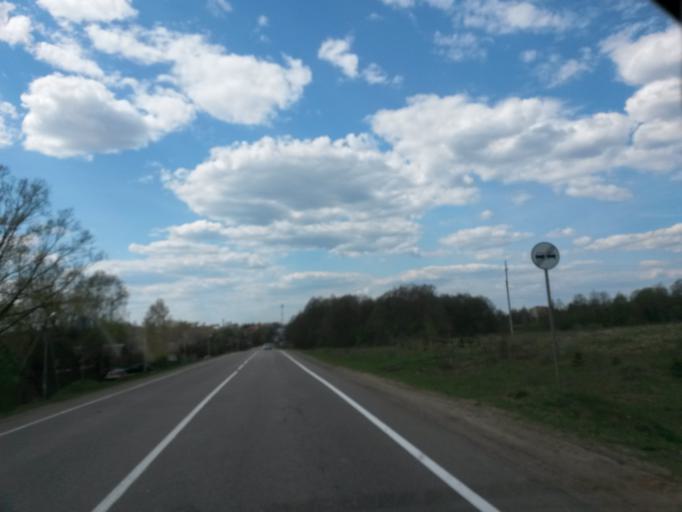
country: RU
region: Jaroslavl
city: Bol'shoye Selo
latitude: 57.7202
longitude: 38.9581
